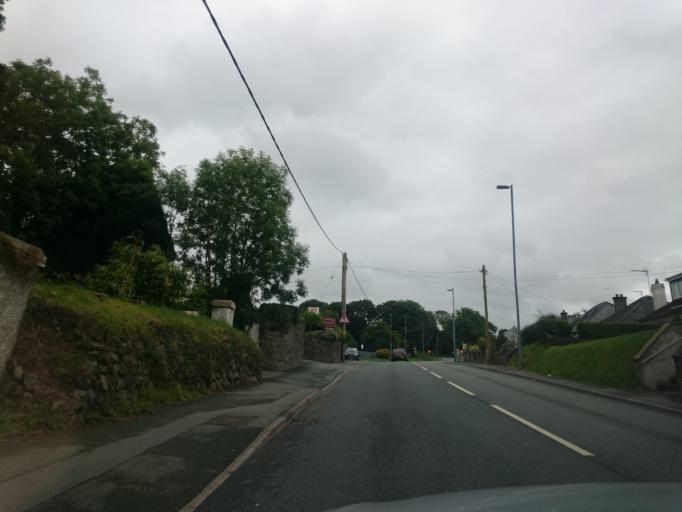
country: GB
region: Wales
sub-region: Pembrokeshire
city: Haverfordwest
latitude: 51.7904
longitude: -4.9764
